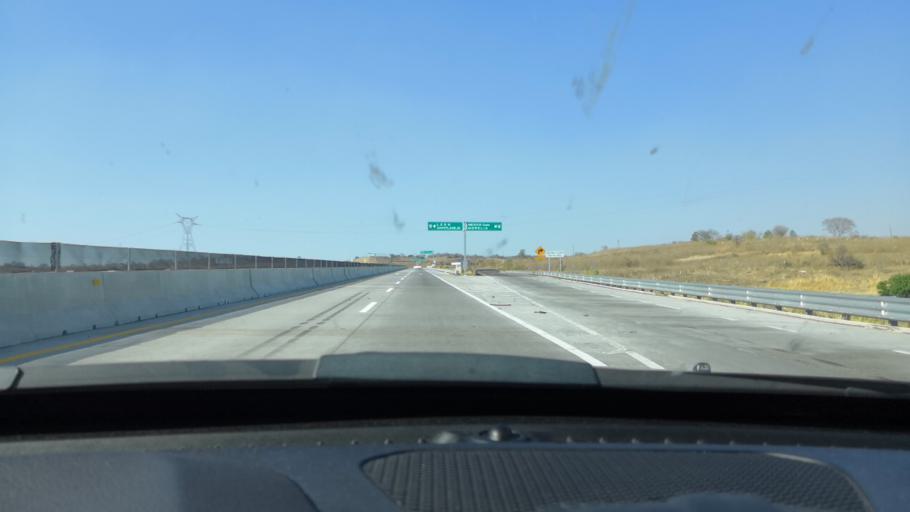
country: MX
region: Jalisco
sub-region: Zapotlanejo
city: La Mezquitera
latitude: 20.5823
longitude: -103.0998
